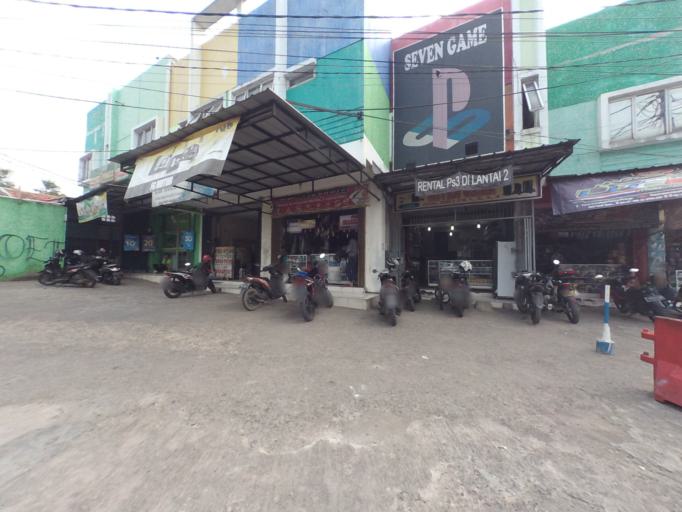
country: ID
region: West Java
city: Ciampea
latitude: -6.5545
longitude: 106.6968
